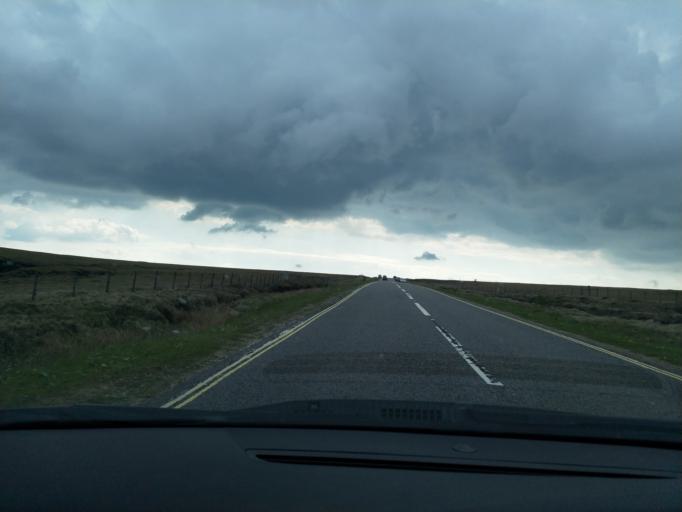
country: GB
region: England
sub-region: Derbyshire
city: High Peak
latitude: 53.4329
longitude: -1.8626
